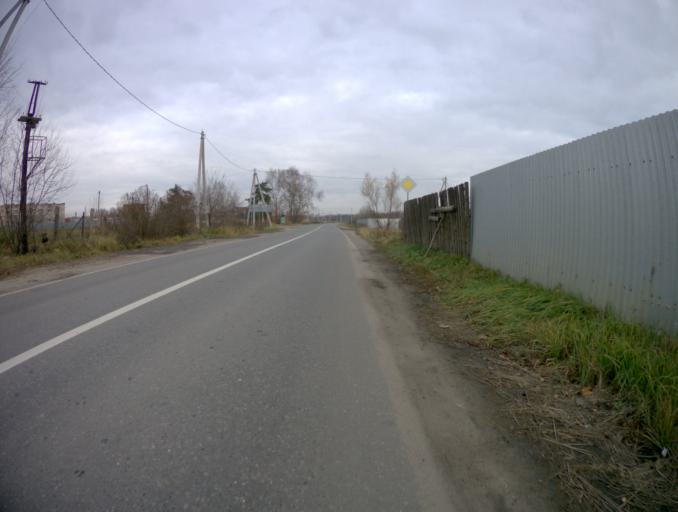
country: RU
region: Moskovskaya
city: Malaya Dubna
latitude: 55.8768
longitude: 38.9618
